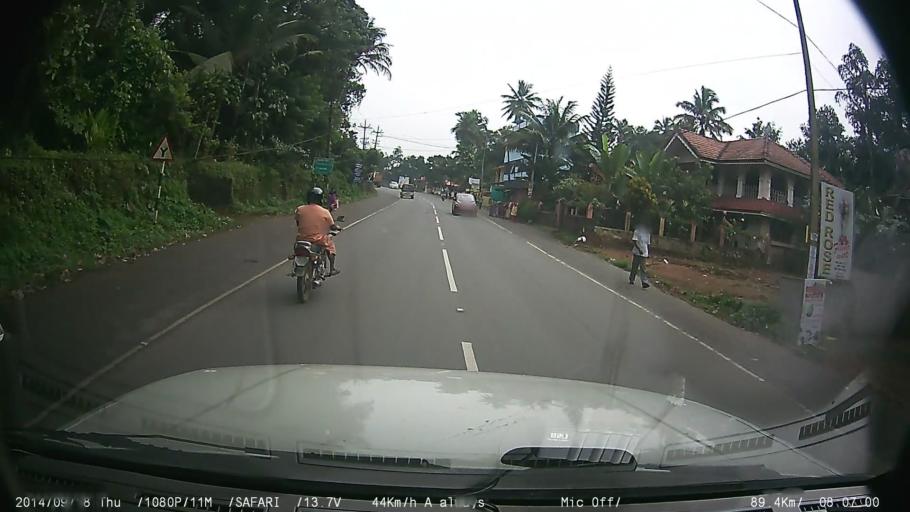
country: IN
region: Kerala
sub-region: Kottayam
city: Kottayam
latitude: 9.5916
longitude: 76.5837
